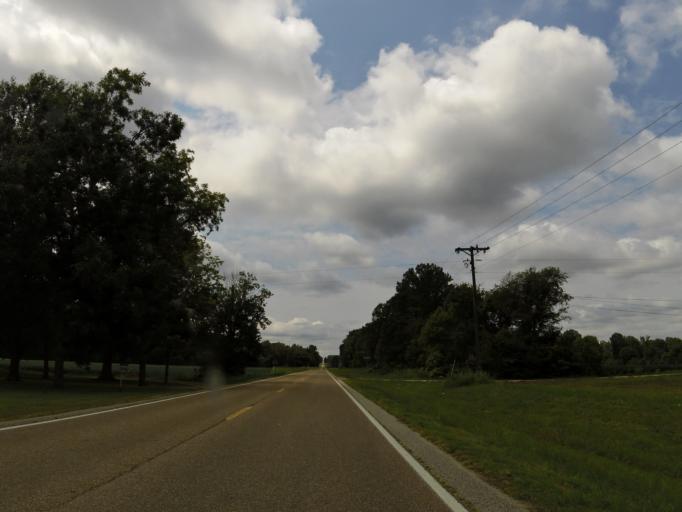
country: US
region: Tennessee
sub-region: Henderson County
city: Lexington
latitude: 35.5155
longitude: -88.2935
